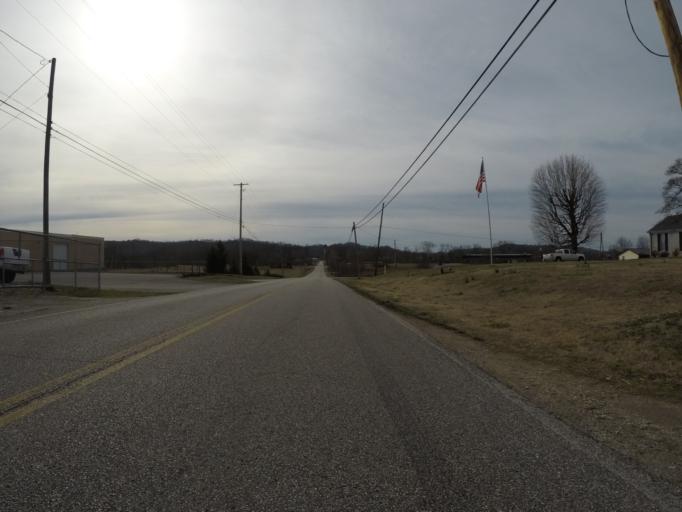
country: US
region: West Virginia
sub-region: Cabell County
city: Pea Ridge
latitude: 38.4462
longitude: -82.3761
